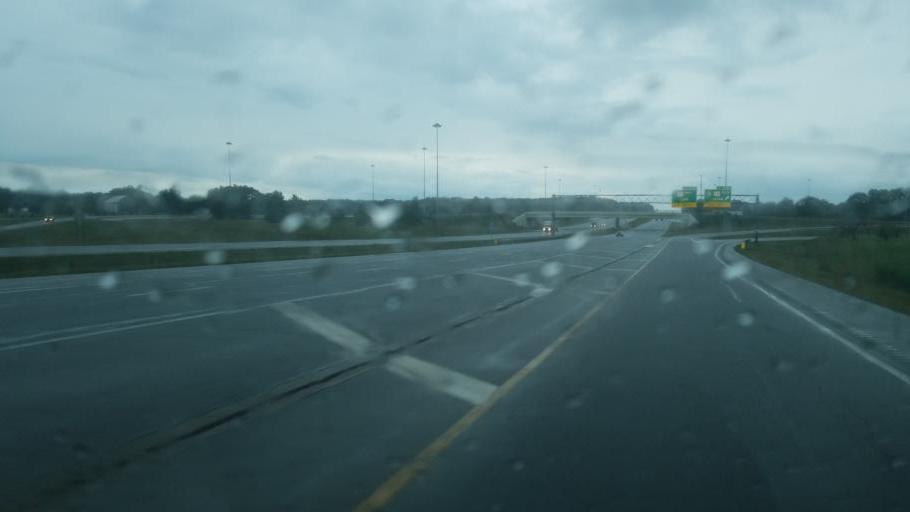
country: US
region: Ohio
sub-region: Medina County
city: Seville
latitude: 41.0293
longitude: -81.8944
